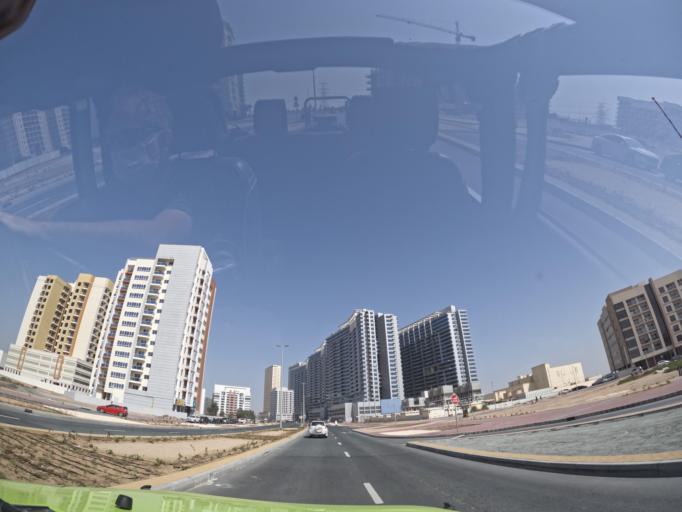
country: AE
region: Dubai
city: Dubai
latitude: 25.0877
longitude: 55.3859
